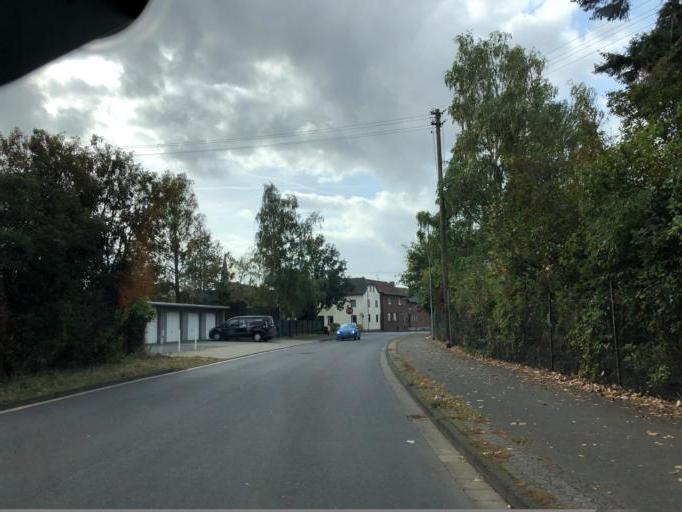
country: DE
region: North Rhine-Westphalia
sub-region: Regierungsbezirk Koln
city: Rheinbach
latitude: 50.6430
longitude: 6.9205
